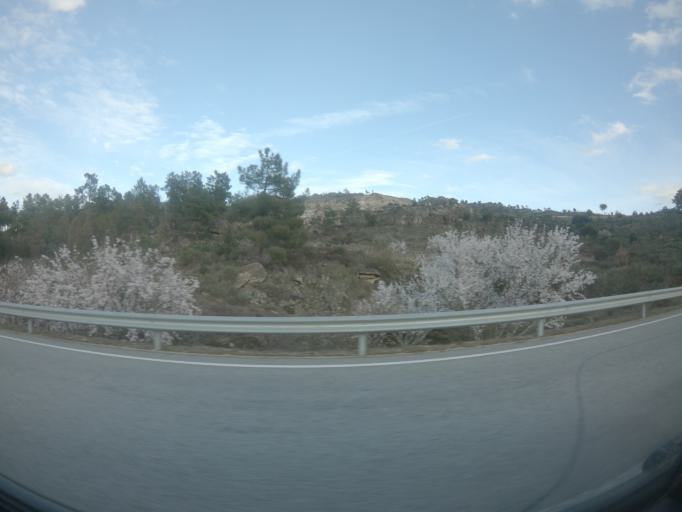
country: PT
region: Braganca
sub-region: Carrazeda de Ansiaes
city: Carrazeda de Anciaes
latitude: 41.2906
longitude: -7.3370
